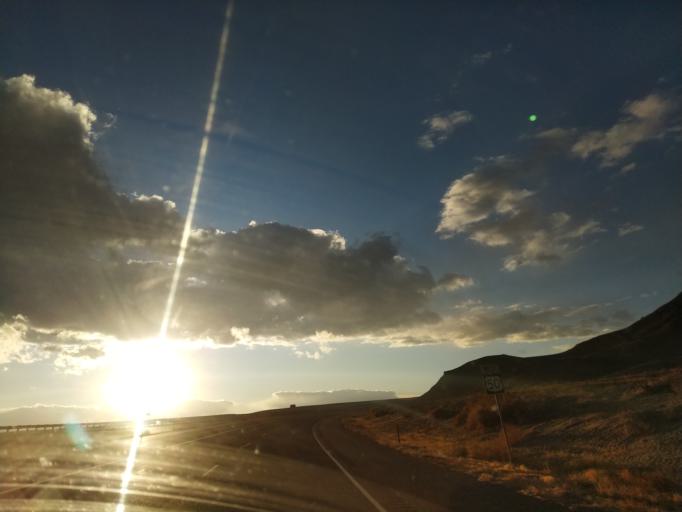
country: US
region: Colorado
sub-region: Delta County
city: Delta
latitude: 38.7520
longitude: -108.1586
